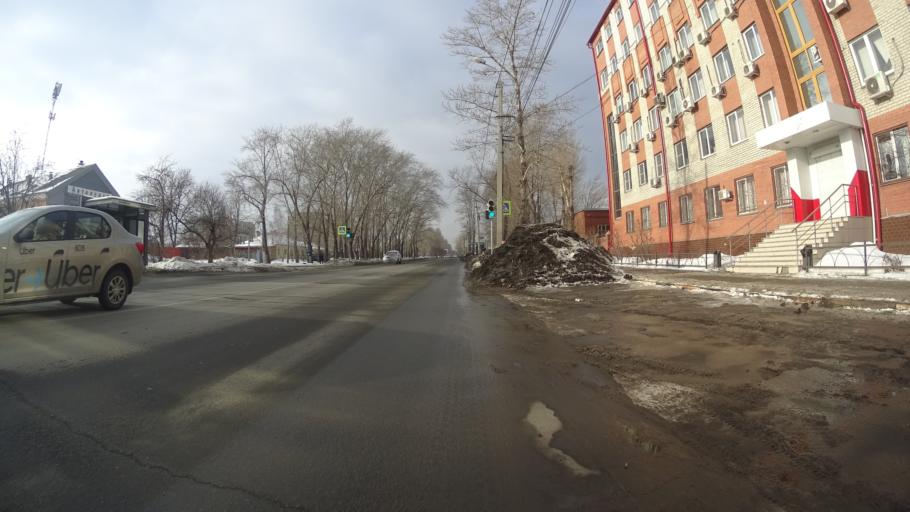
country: RU
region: Chelyabinsk
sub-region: Gorod Chelyabinsk
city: Chelyabinsk
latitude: 55.1213
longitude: 61.3782
